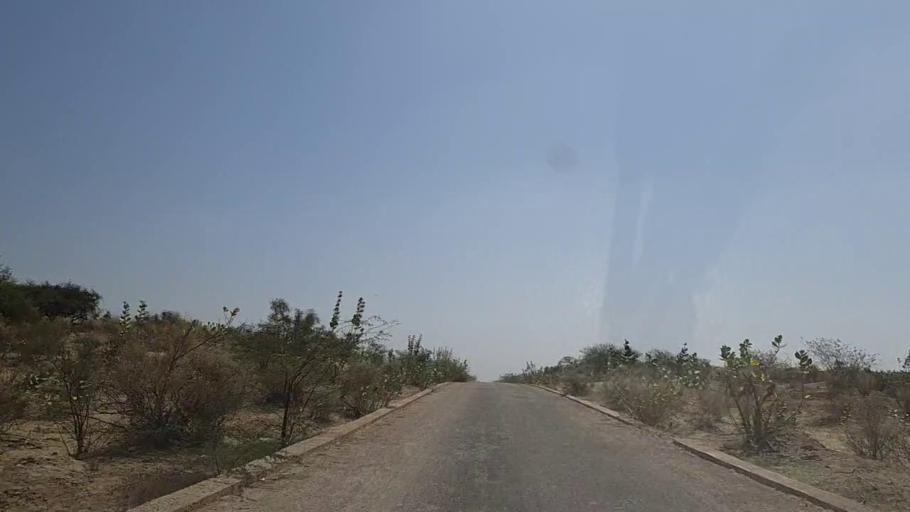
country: PK
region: Sindh
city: Diplo
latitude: 24.5049
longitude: 69.4255
